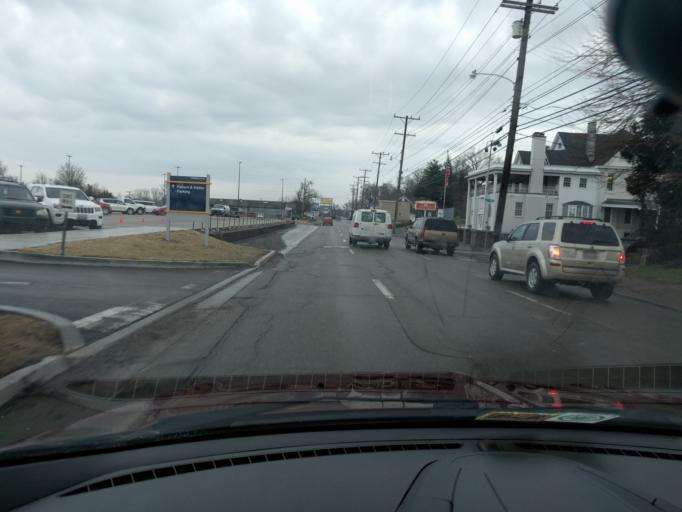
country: US
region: West Virginia
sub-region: Wood County
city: Parkersburg
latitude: 39.2710
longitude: -81.5580
